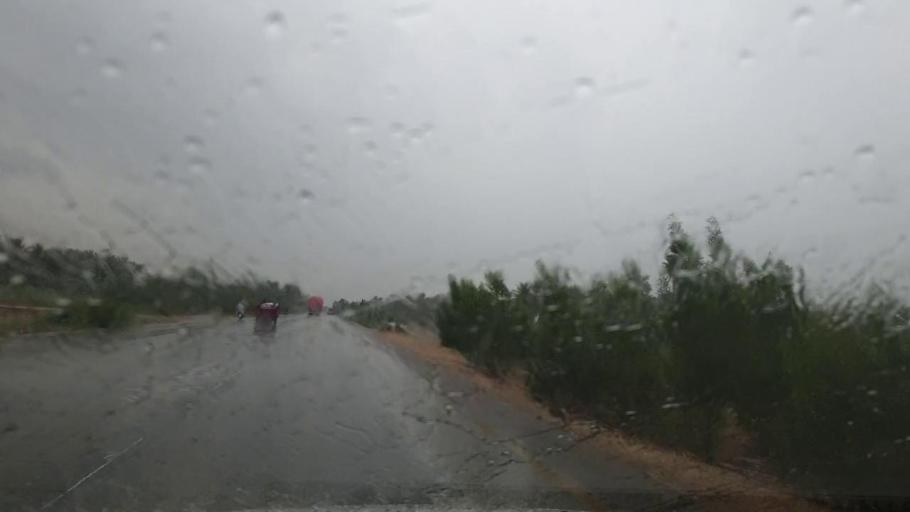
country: PK
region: Sindh
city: Khairpur
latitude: 27.5498
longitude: 68.7317
